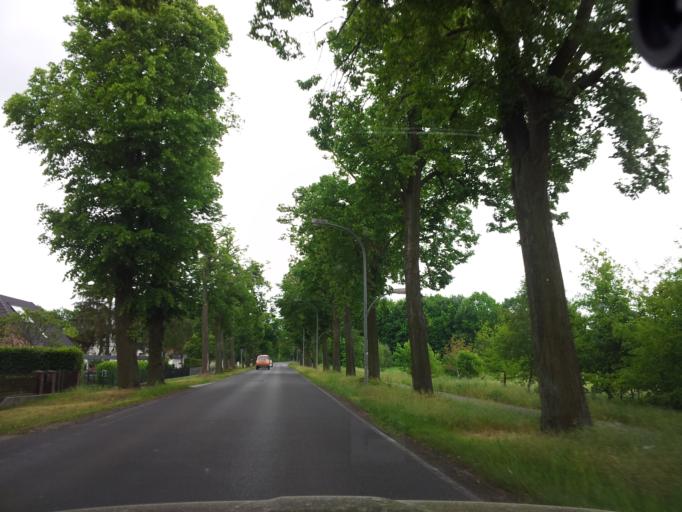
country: DE
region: Brandenburg
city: Dallgow-Doeberitz
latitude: 52.5470
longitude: 13.0621
